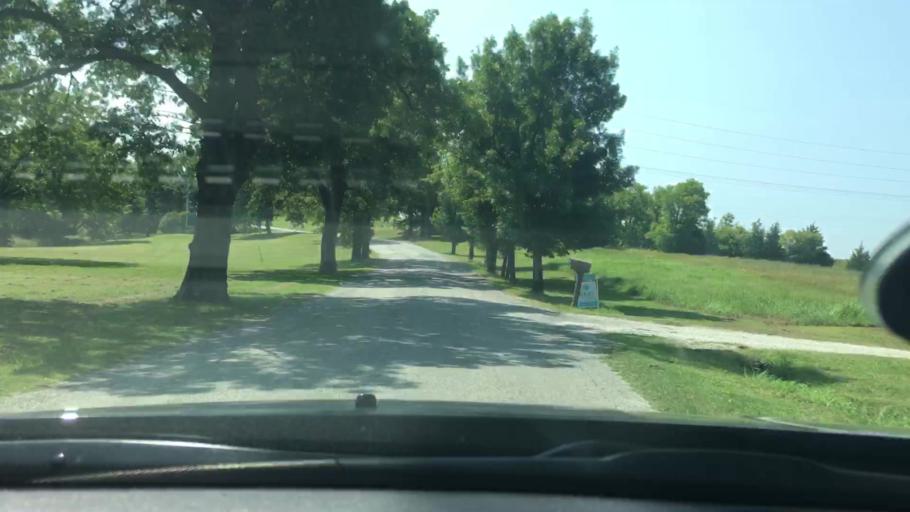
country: US
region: Oklahoma
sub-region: Pontotoc County
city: Ada
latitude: 34.7832
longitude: -96.6002
